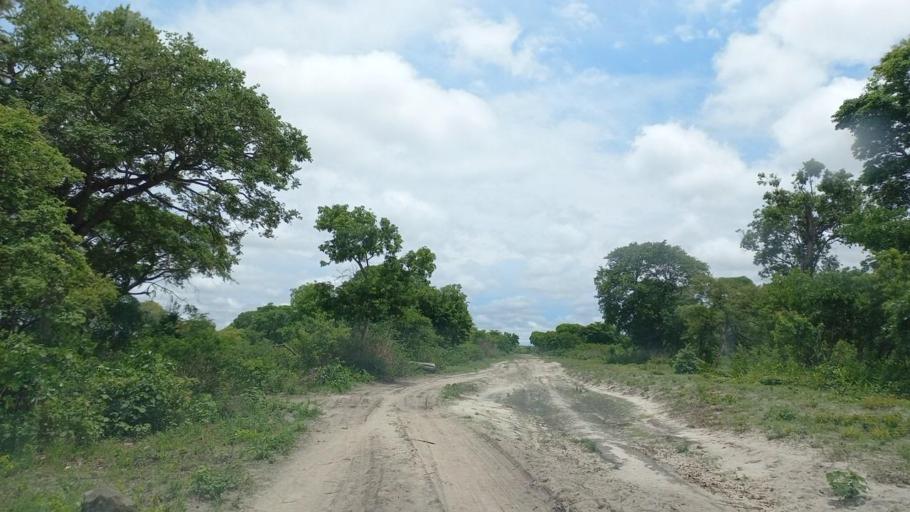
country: ZM
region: North-Western
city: Kabompo
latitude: -13.1781
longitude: 23.9470
